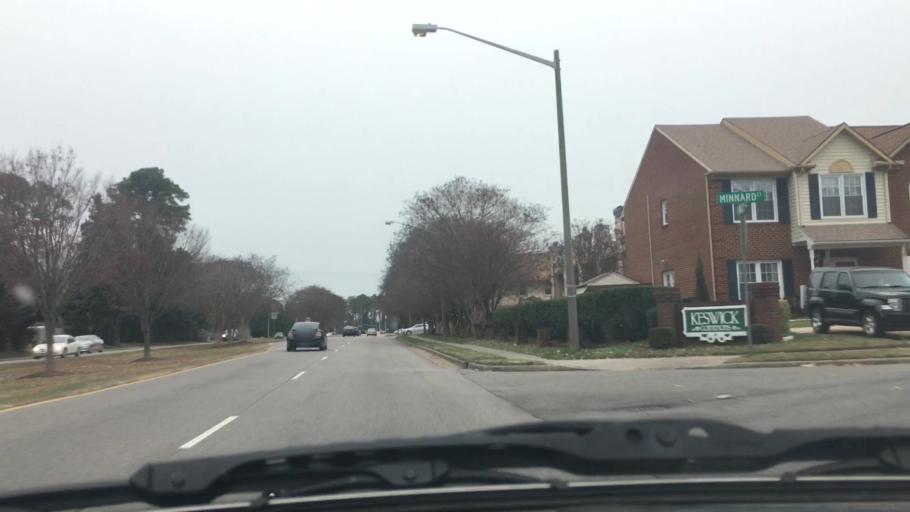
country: US
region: Virginia
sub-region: City of Chesapeake
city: Chesapeake
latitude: 36.8183
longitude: -76.1268
